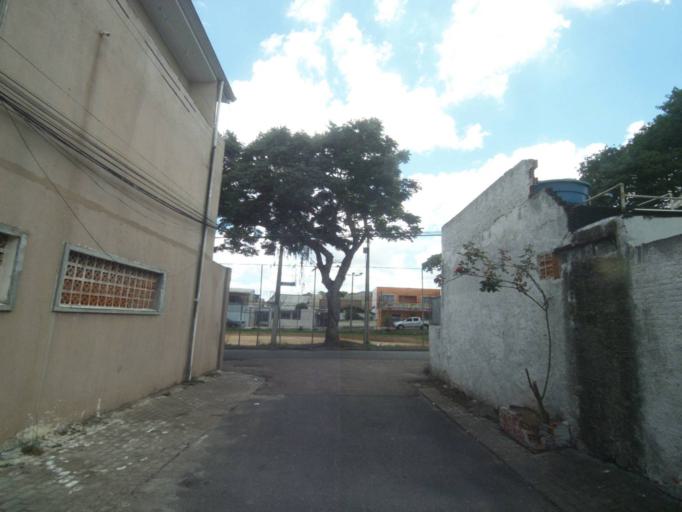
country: BR
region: Parana
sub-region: Curitiba
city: Curitiba
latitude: -25.5091
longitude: -49.3241
